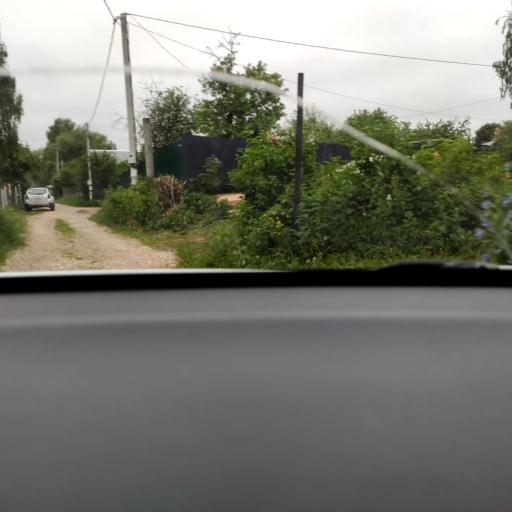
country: RU
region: Tatarstan
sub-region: Gorod Kazan'
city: Kazan
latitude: 55.8876
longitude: 49.0602
